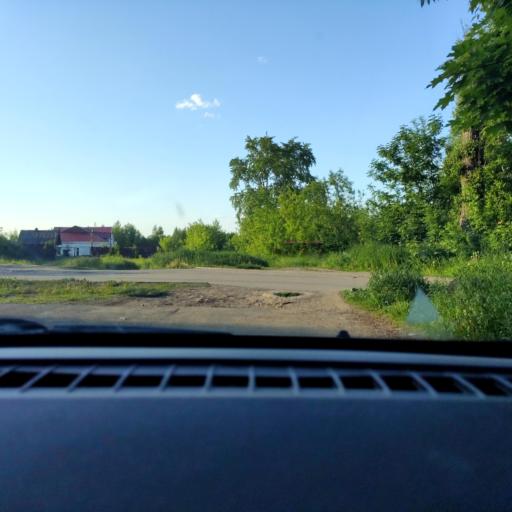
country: RU
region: Perm
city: Polazna
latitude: 58.1386
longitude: 56.3860
